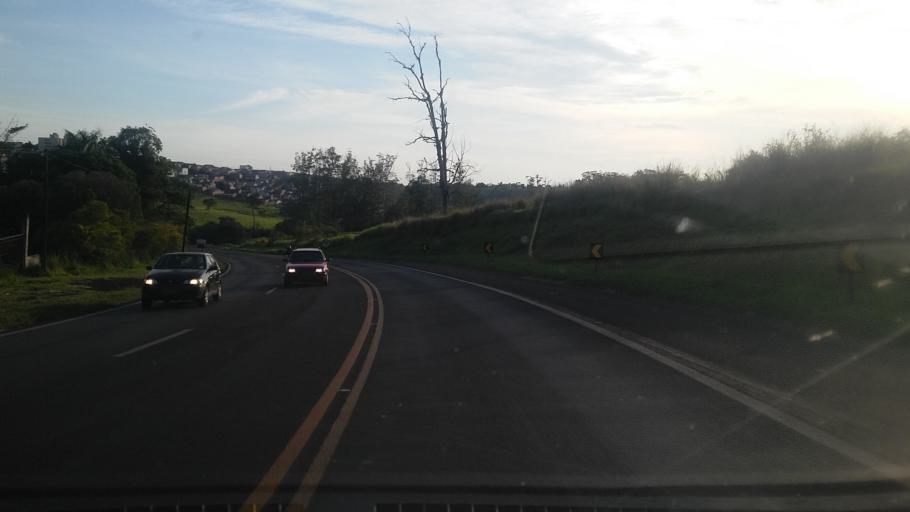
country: BR
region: Parana
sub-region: Bandeirantes
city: Bandeirantes
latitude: -23.1828
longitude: -50.6330
